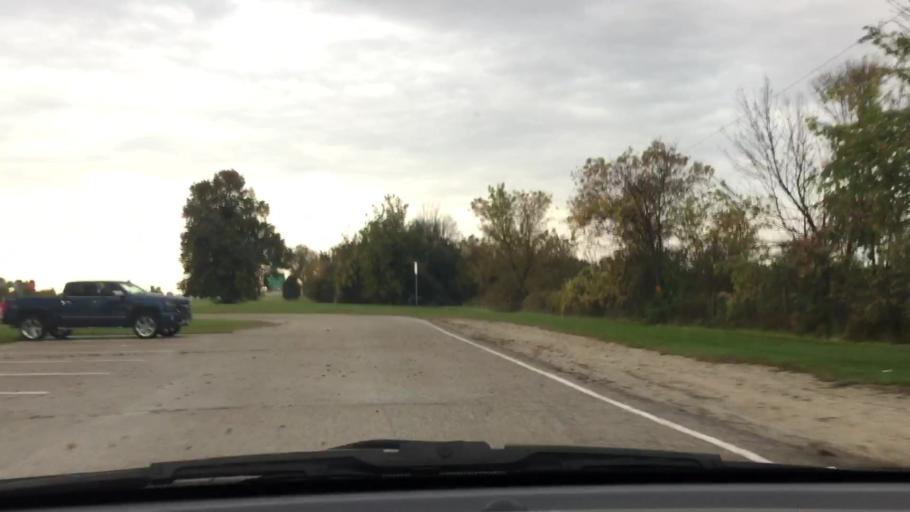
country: US
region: Wisconsin
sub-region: Walworth County
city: Elkhorn
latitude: 42.7026
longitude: -88.5424
